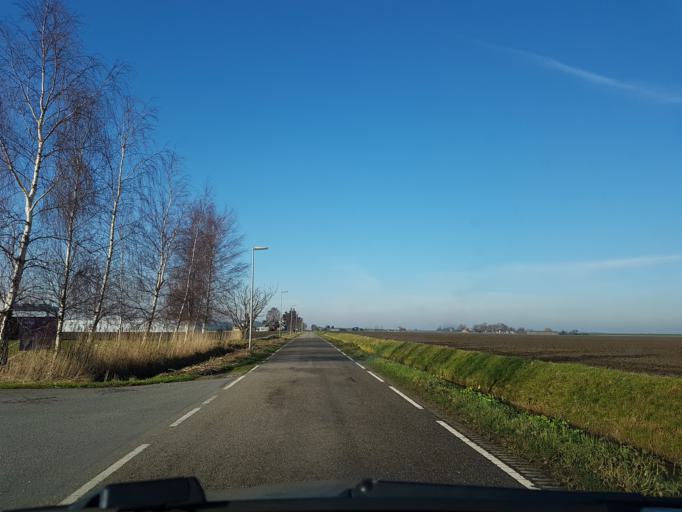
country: NL
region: South Holland
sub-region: Gemeente Waddinxveen
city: Groenswaard
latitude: 52.0388
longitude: 4.6179
